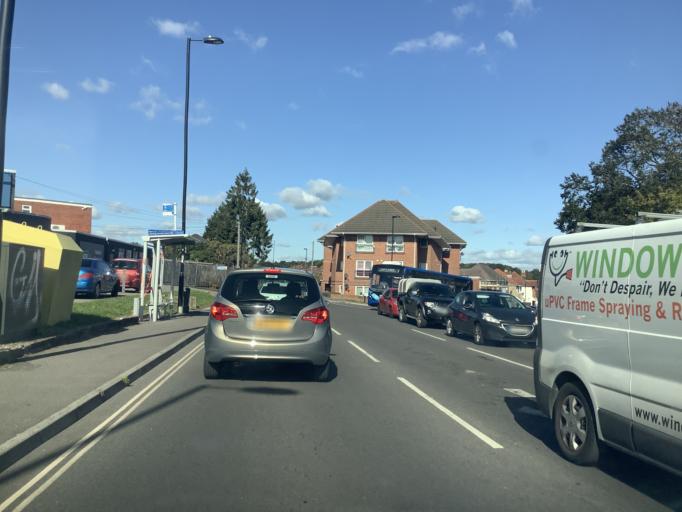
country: GB
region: England
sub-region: Hampshire
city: Marchwood
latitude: 50.9311
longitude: -1.4479
